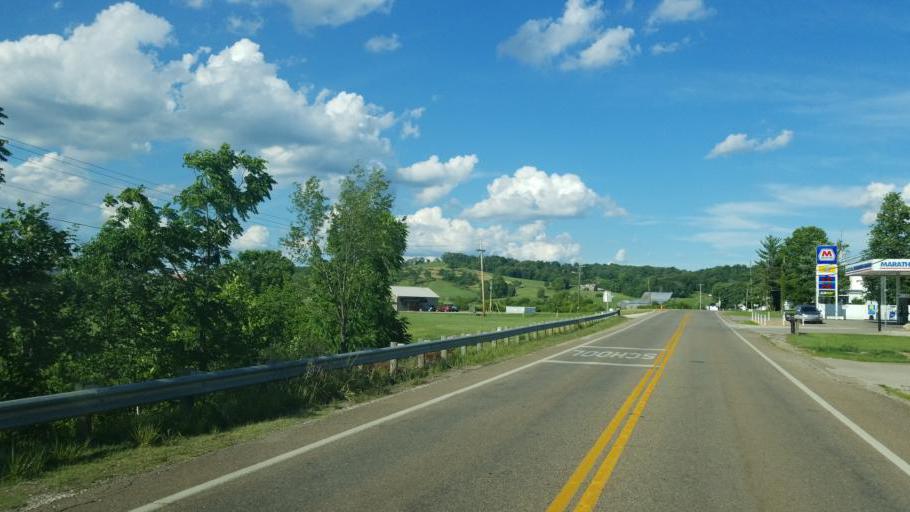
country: US
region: Ohio
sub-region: Gallia County
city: Gallipolis
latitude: 38.7996
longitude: -82.2661
